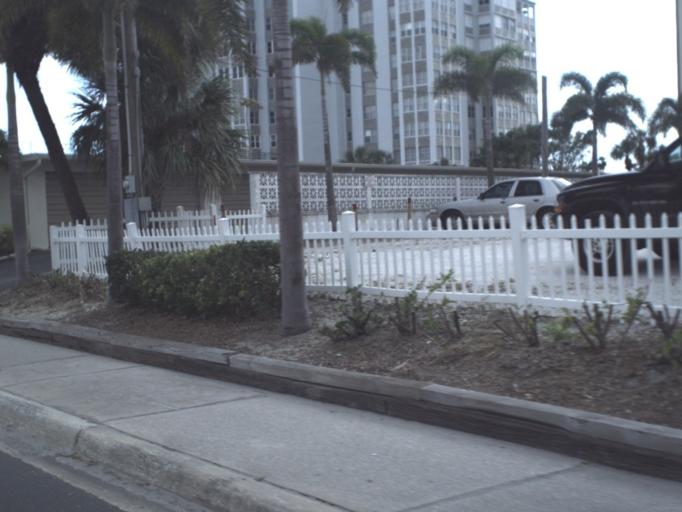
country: US
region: Florida
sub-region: Pinellas County
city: Saint Pete Beach
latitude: 27.7245
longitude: -82.7412
